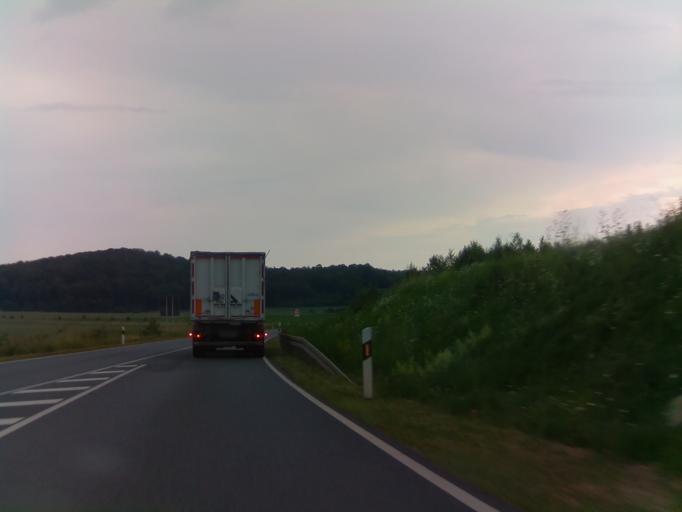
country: DE
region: Lower Saxony
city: Elze
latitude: 52.1159
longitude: 9.6849
